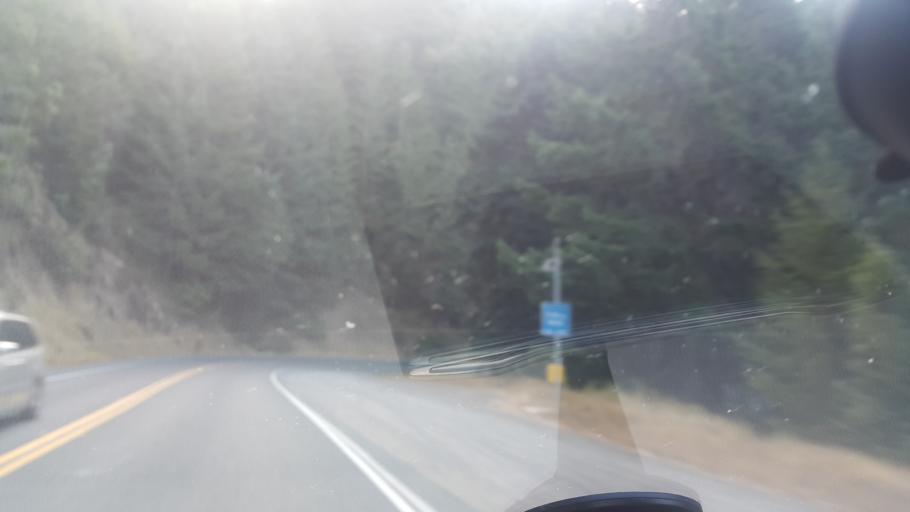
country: US
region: California
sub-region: Mendocino County
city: Brooktrails
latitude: 39.3709
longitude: -123.4969
